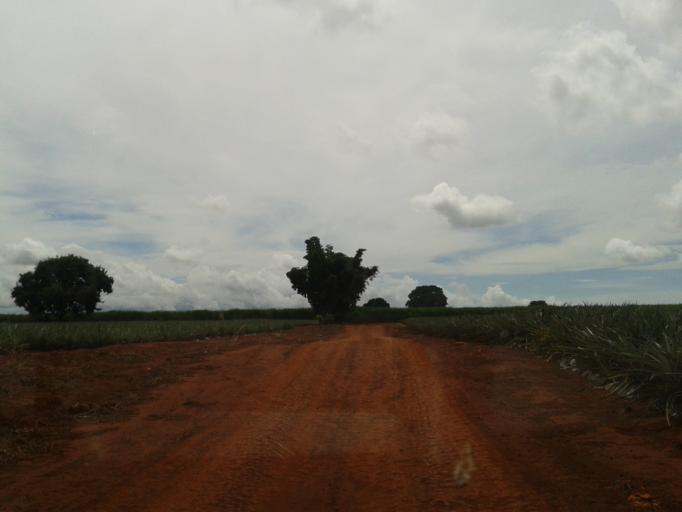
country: BR
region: Minas Gerais
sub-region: Centralina
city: Centralina
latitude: -18.5861
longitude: -49.2688
